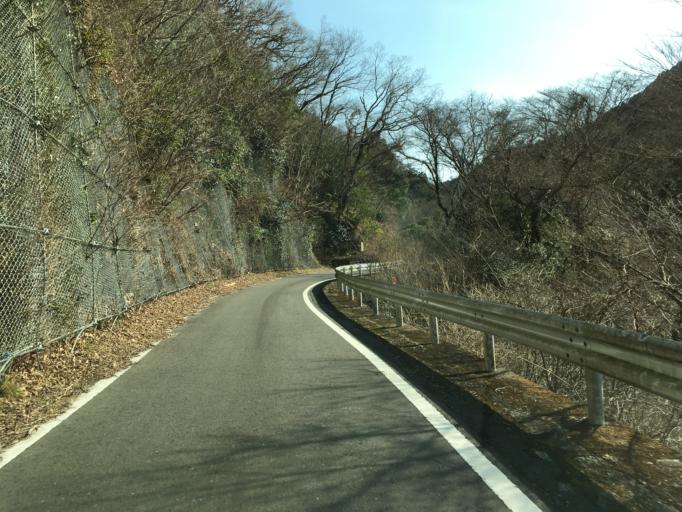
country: JP
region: Ibaraki
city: Kitaibaraki
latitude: 36.7837
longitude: 140.6765
